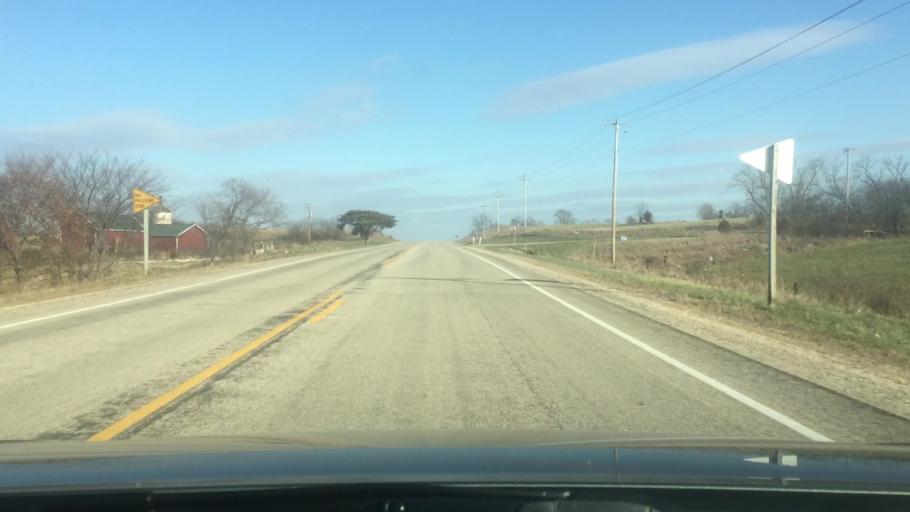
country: US
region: Wisconsin
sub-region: Jefferson County
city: Palmyra
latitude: 42.9330
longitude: -88.6469
